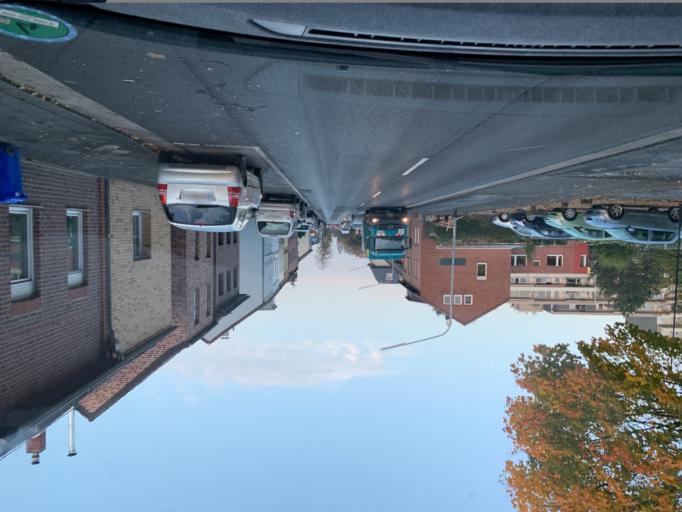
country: DE
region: North Rhine-Westphalia
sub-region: Regierungsbezirk Dusseldorf
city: Juchen
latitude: 51.1261
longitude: 6.4547
